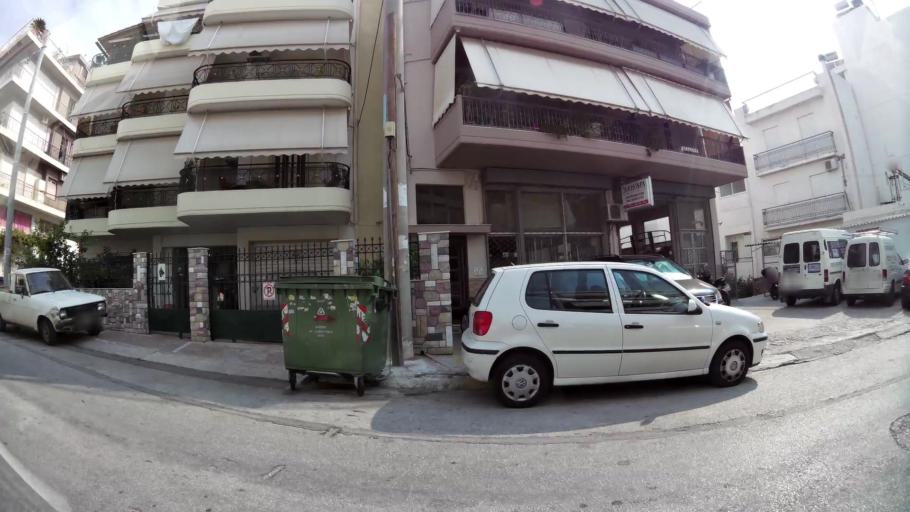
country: GR
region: Attica
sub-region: Nomarchia Athinas
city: Alimos
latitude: 37.9224
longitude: 23.7266
